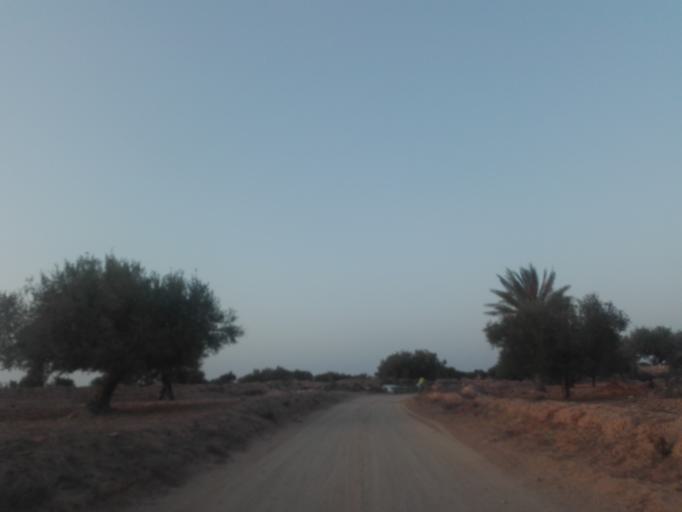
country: TN
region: Madanin
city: Houmt Souk
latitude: 33.7412
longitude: 10.7648
